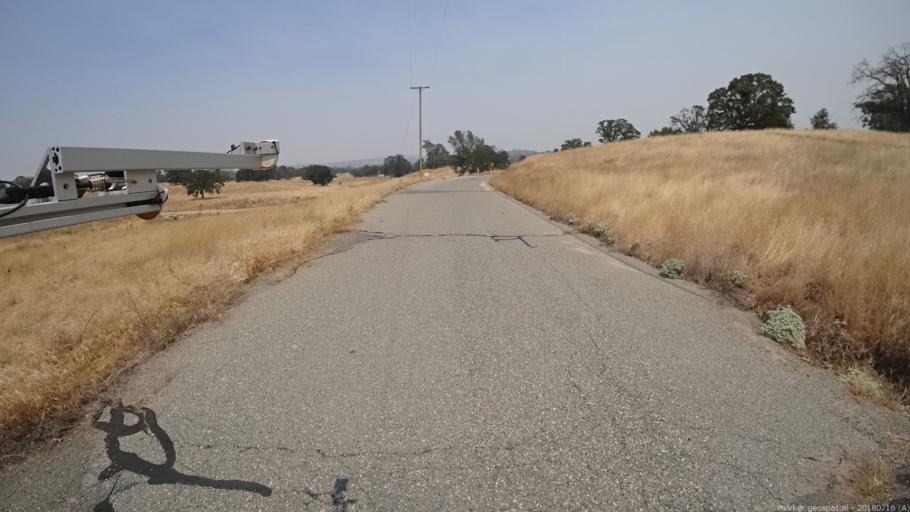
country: US
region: California
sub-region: Madera County
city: Yosemite Lakes
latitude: 37.1945
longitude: -119.9033
